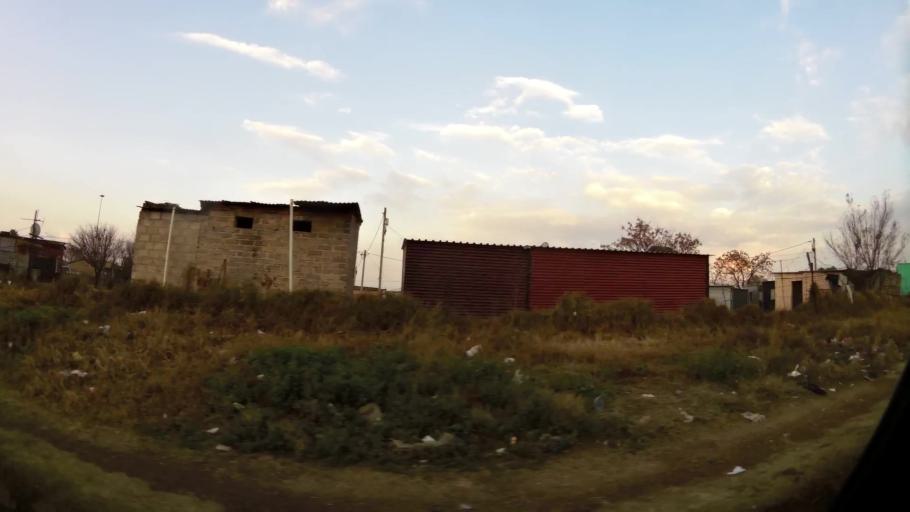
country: ZA
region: Gauteng
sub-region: City of Johannesburg Metropolitan Municipality
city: Orange Farm
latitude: -26.5530
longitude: 27.8400
